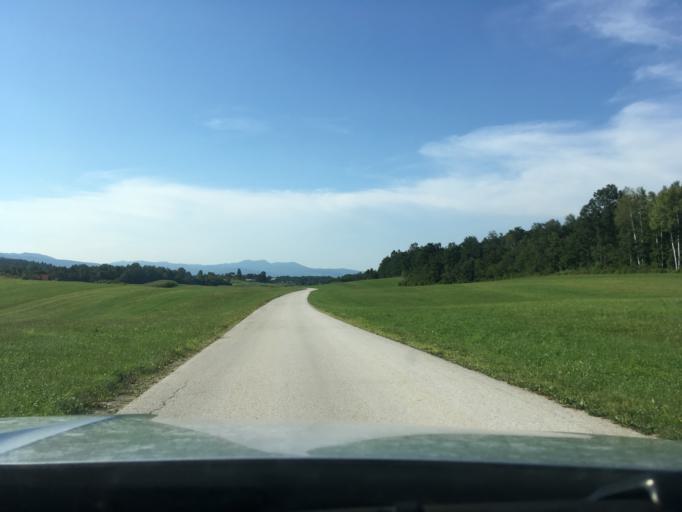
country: SI
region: Crnomelj
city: Crnomelj
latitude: 45.4612
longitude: 15.2139
